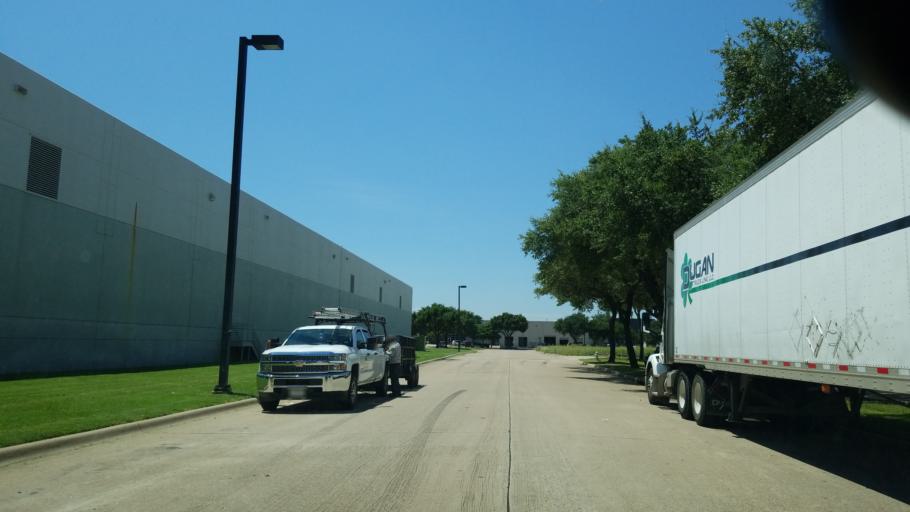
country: US
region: Texas
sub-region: Dallas County
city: Farmers Branch
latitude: 32.9421
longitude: -96.9270
